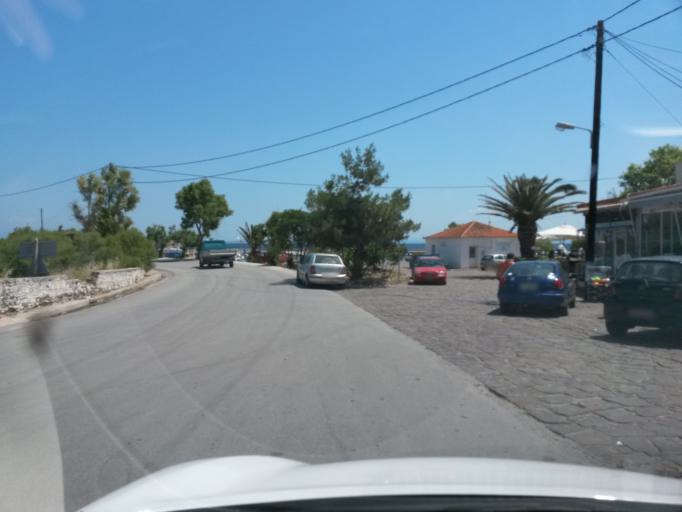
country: GR
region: North Aegean
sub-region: Nomos Lesvou
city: Pamfylla
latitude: 39.1815
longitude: 26.4981
